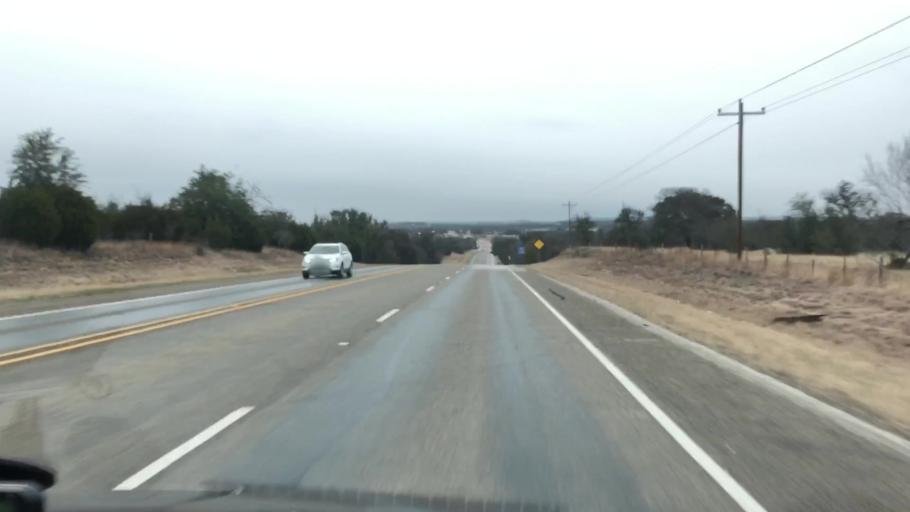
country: US
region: Texas
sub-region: Lampasas County
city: Lampasas
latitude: 31.2859
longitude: -98.1709
